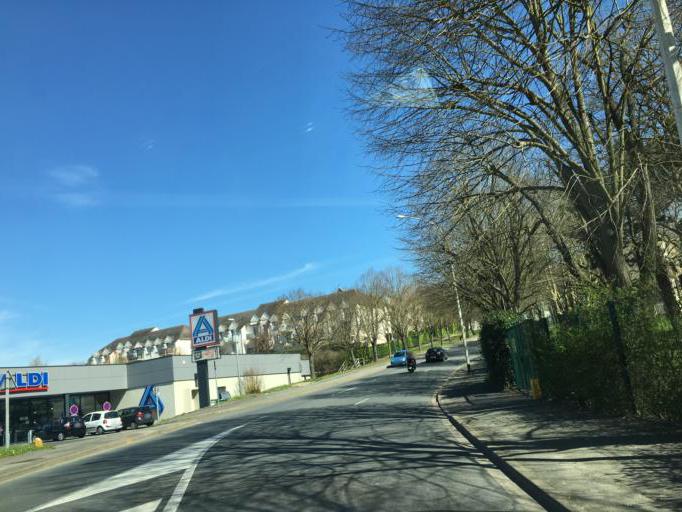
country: FR
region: Ile-de-France
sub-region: Departement de l'Essonne
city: Ris-Orangis
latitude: 48.6630
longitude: 2.4178
